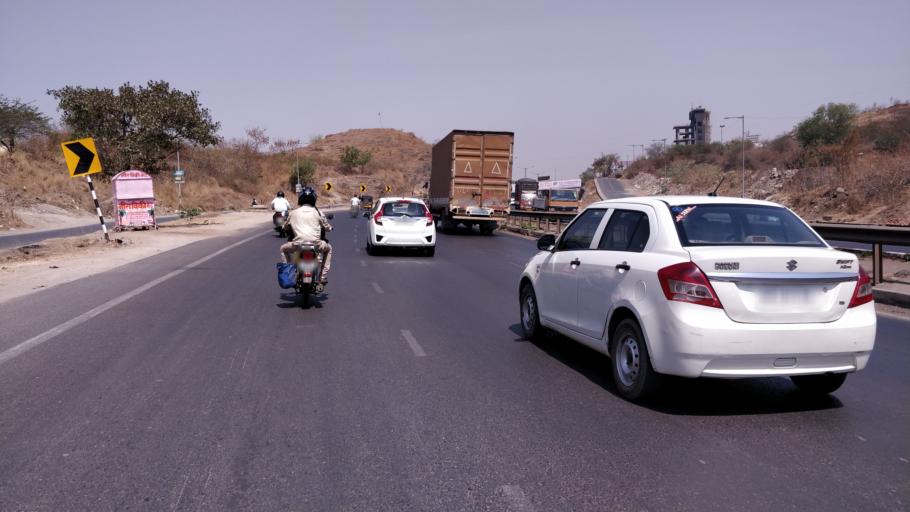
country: IN
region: Maharashtra
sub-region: Pune Division
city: Shivaji Nagar
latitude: 18.5443
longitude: 73.7749
